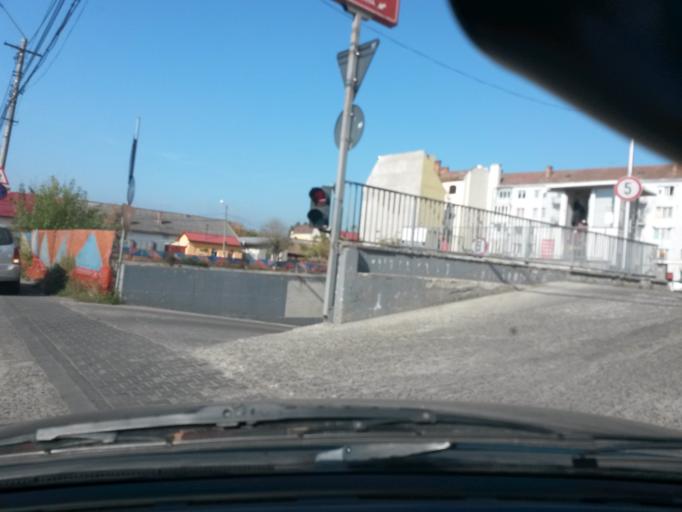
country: RO
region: Mures
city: Targu-Mures
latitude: 46.5395
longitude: 24.5573
